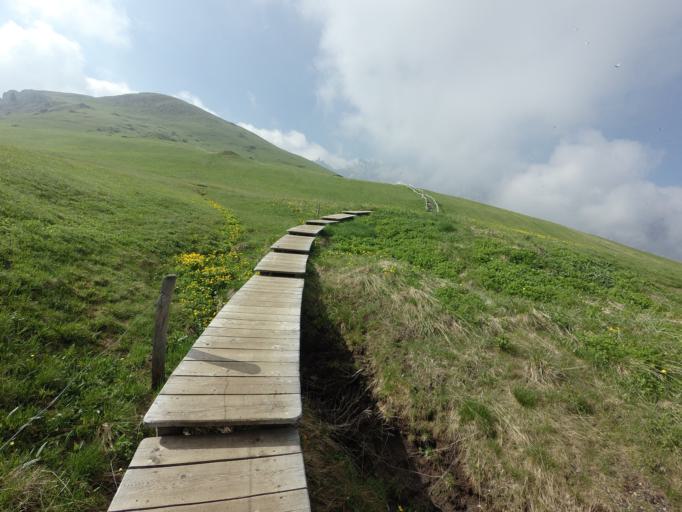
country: IT
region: Trentino-Alto Adige
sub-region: Bolzano
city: Ortisei
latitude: 46.5213
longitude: 11.6322
